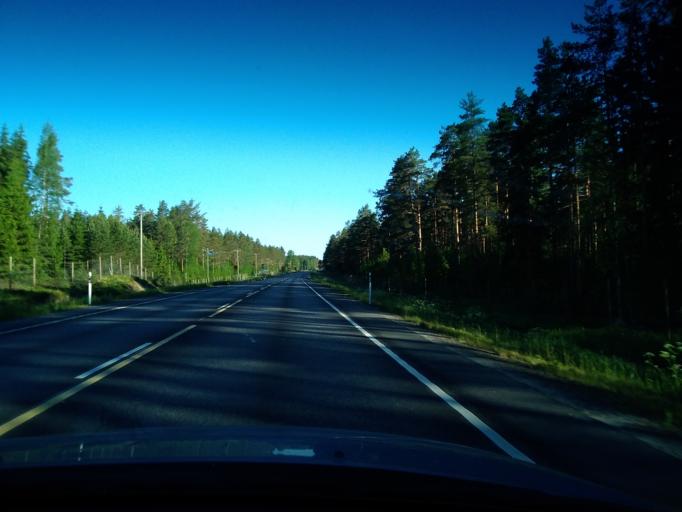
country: FI
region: Uusimaa
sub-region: Helsinki
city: Kaerkoelae
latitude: 60.6447
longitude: 23.8766
